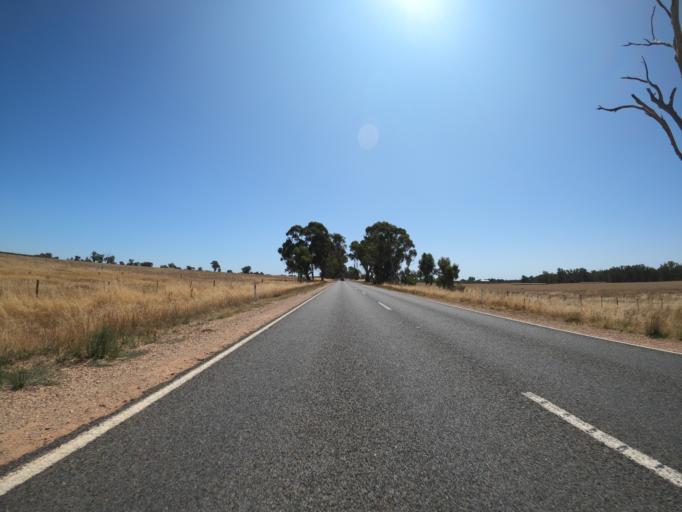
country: AU
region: Victoria
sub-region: Moira
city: Yarrawonga
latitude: -36.0684
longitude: 146.1892
